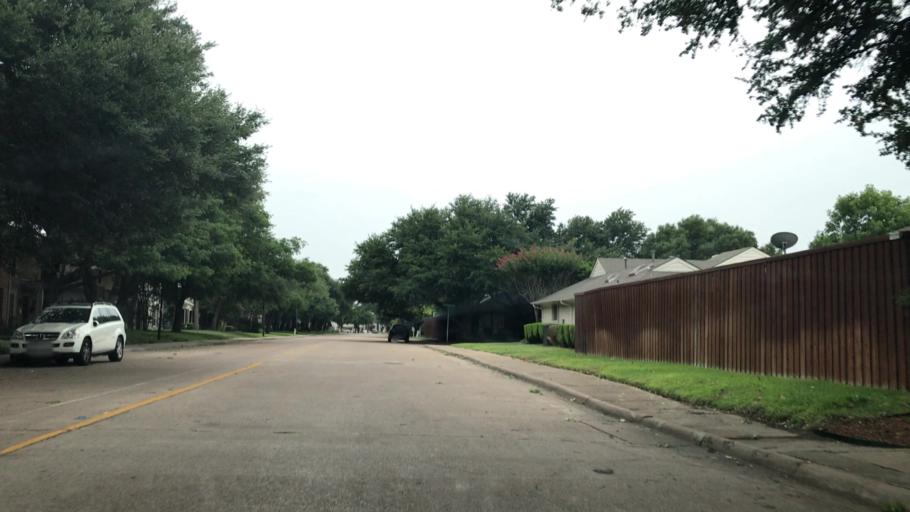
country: US
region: Texas
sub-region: Dallas County
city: Addison
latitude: 32.9670
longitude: -96.7914
